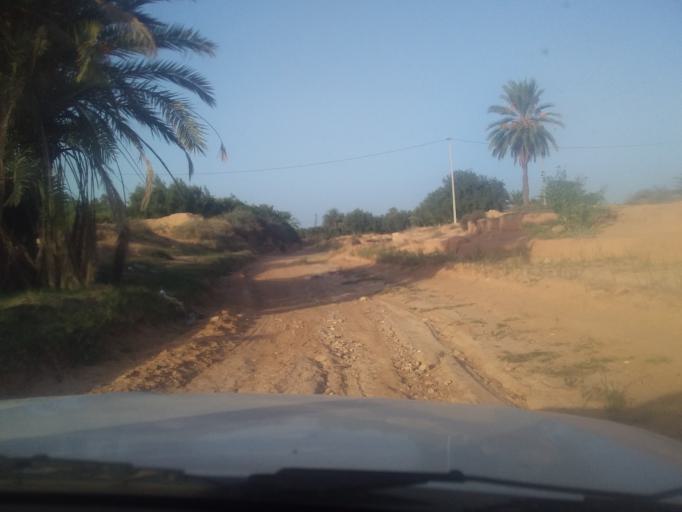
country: TN
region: Qabis
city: Gabes
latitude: 33.6286
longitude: 10.2978
